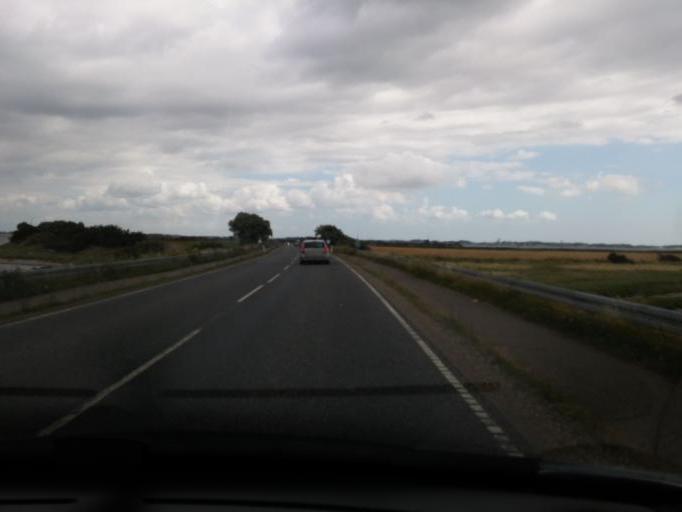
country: DK
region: South Denmark
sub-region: Langeland Kommune
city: Rudkobing
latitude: 54.9610
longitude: 10.6652
